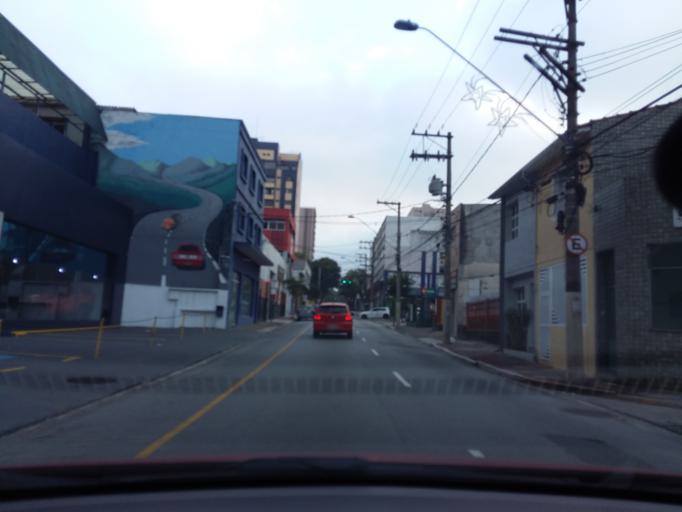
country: BR
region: Sao Paulo
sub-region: Sao Caetano Do Sul
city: Sao Caetano do Sul
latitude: -23.6180
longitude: -46.5679
